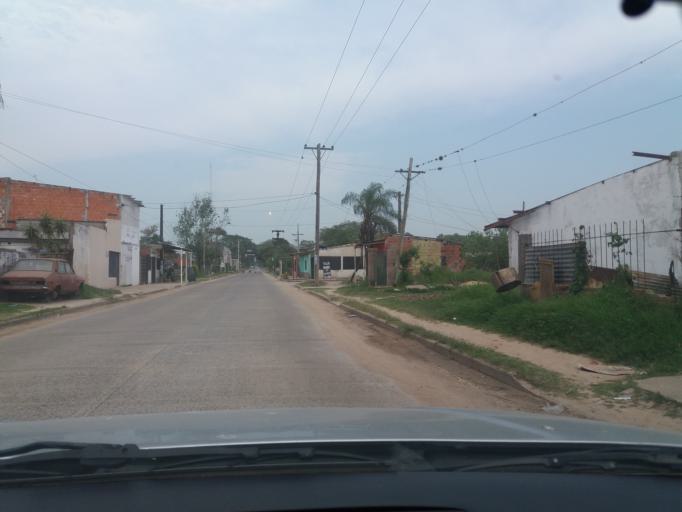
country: AR
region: Corrientes
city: Corrientes
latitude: -27.5124
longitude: -58.8027
